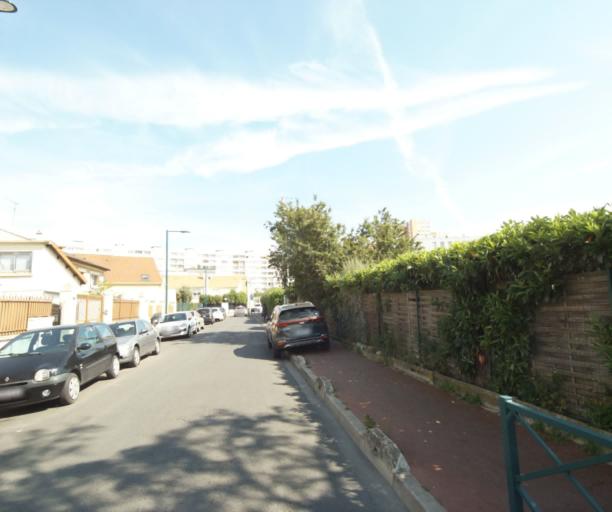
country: FR
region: Ile-de-France
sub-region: Departement des Hauts-de-Seine
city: Gennevilliers
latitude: 48.9312
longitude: 2.2916
